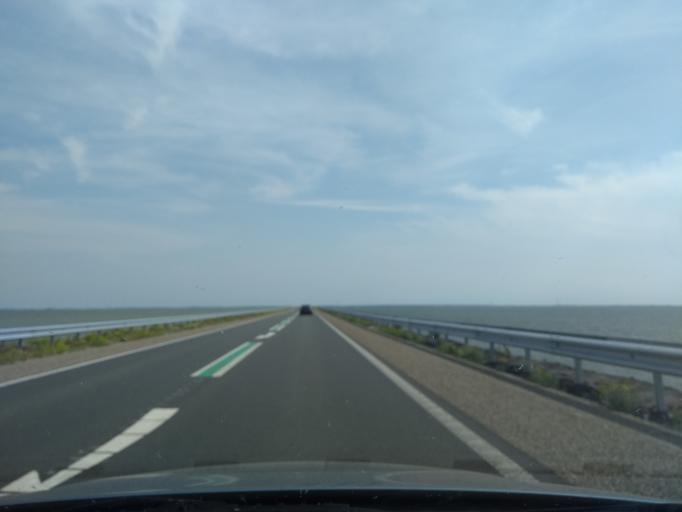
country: NL
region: Flevoland
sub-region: Gemeente Lelystad
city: Lelystad
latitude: 52.6318
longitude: 5.4170
